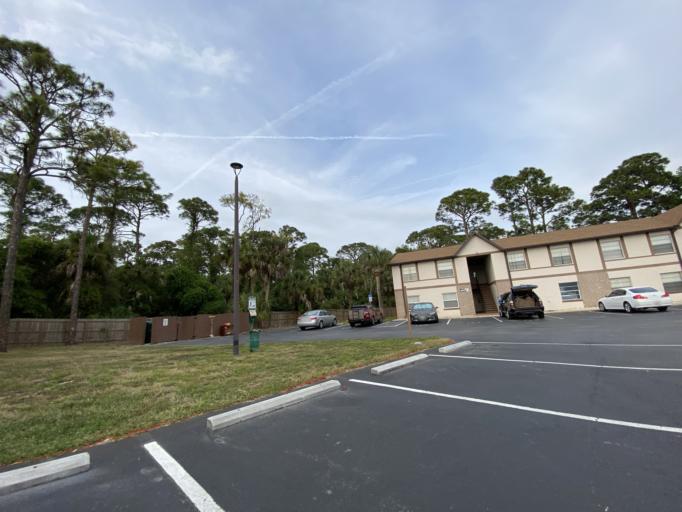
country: US
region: Florida
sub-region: Volusia County
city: South Daytona
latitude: 29.1610
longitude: -80.9999
